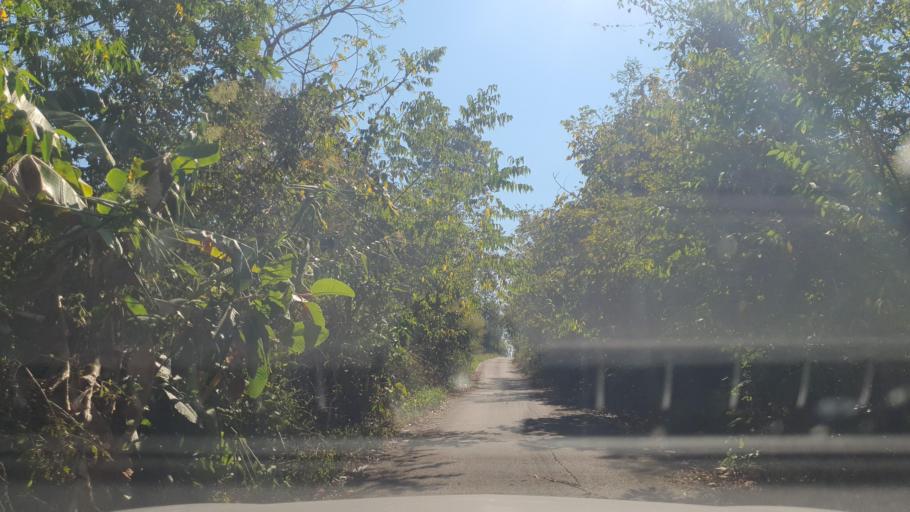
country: TH
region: Chiang Mai
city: Mae On
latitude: 18.8734
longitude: 99.2641
